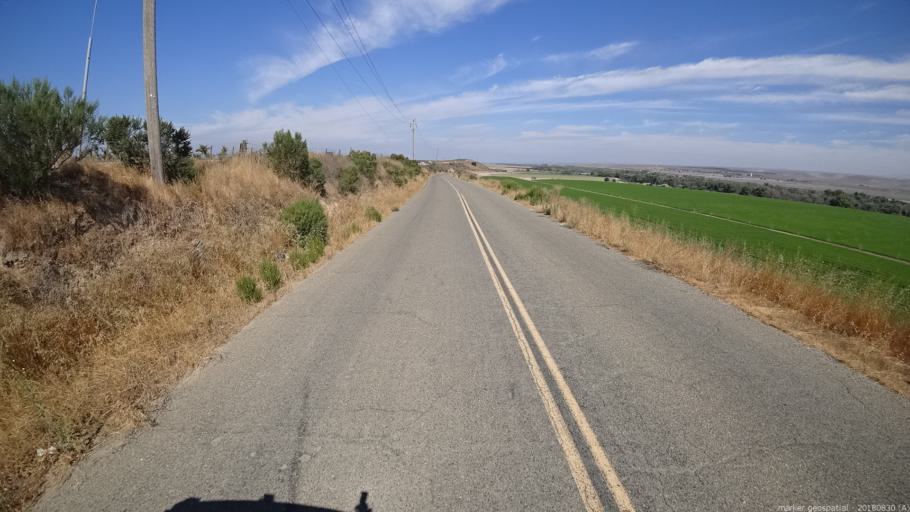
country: US
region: California
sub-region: Monterey County
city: King City
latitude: 36.0963
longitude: -121.0194
